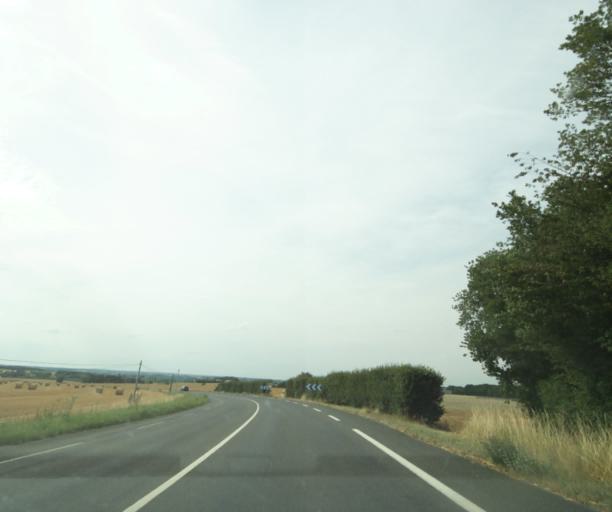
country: FR
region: Centre
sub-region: Departement d'Indre-et-Loire
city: Saint-Christophe-sur-le-Nais
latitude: 47.6534
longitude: 0.4904
